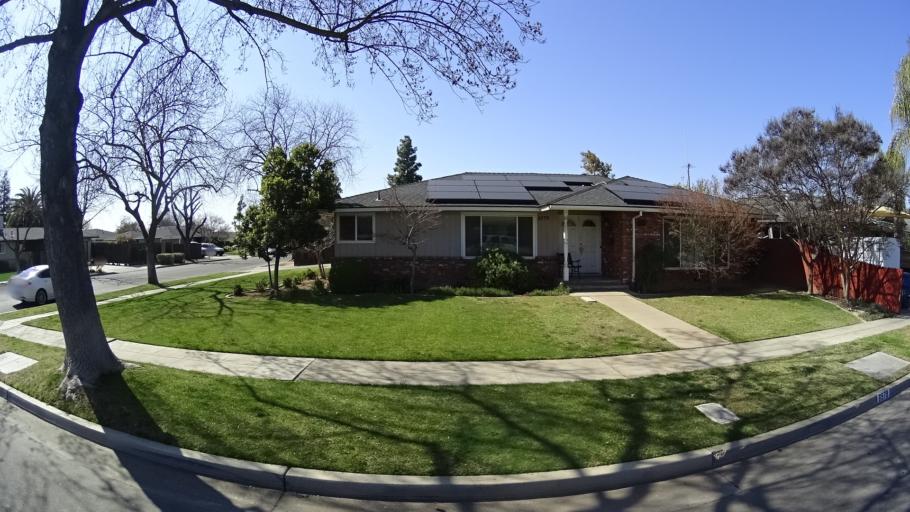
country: US
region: California
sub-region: Fresno County
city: Clovis
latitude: 36.8335
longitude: -119.7792
